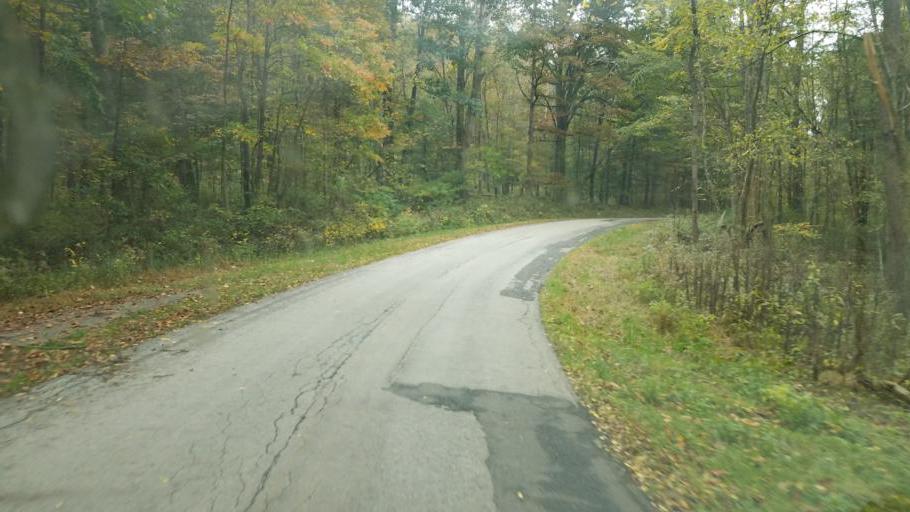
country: US
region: Ohio
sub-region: Ashland County
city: Loudonville
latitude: 40.5603
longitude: -82.1527
